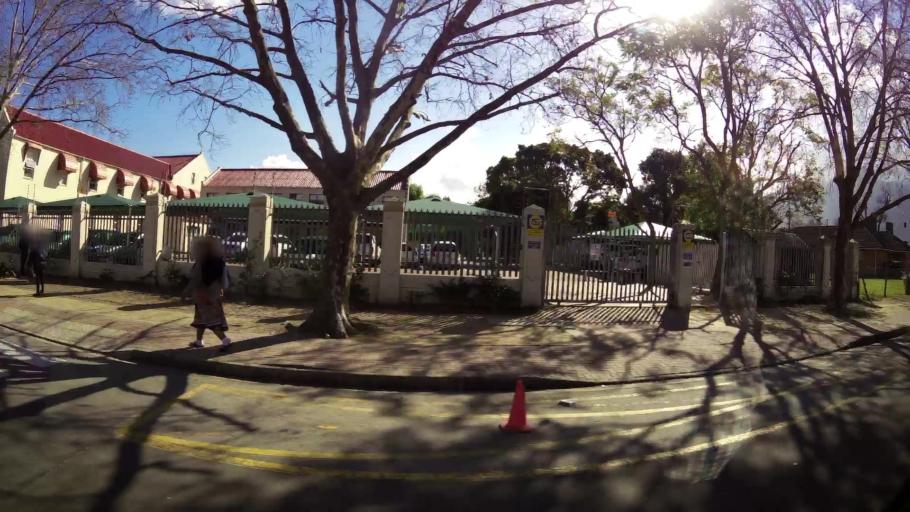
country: ZA
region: Western Cape
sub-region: Eden District Municipality
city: George
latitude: -33.9592
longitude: 22.4606
